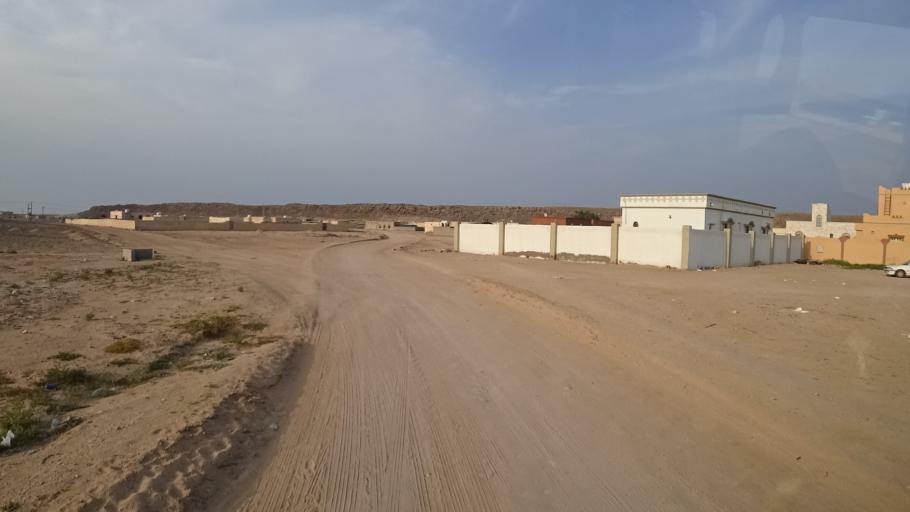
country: OM
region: Ash Sharqiyah
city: Sur
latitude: 22.4348
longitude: 59.8263
